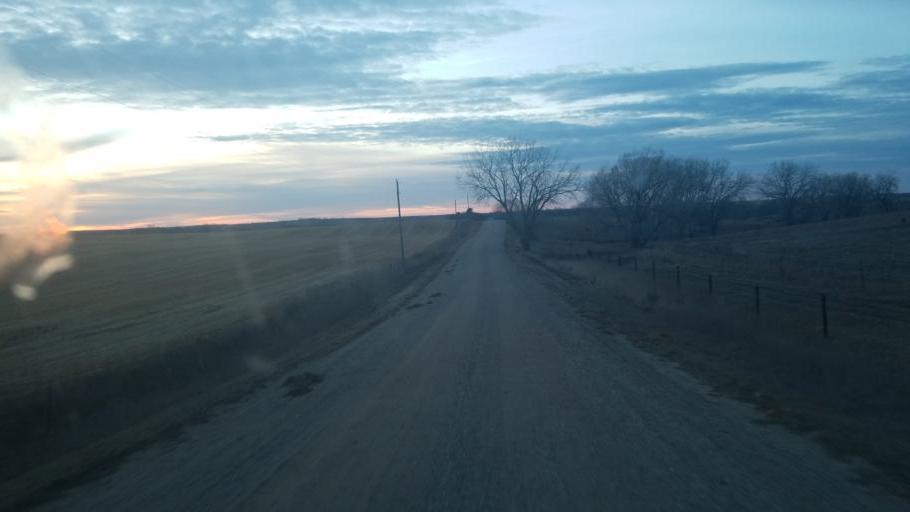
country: US
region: Nebraska
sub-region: Knox County
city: Center
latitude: 42.6554
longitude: -97.7643
